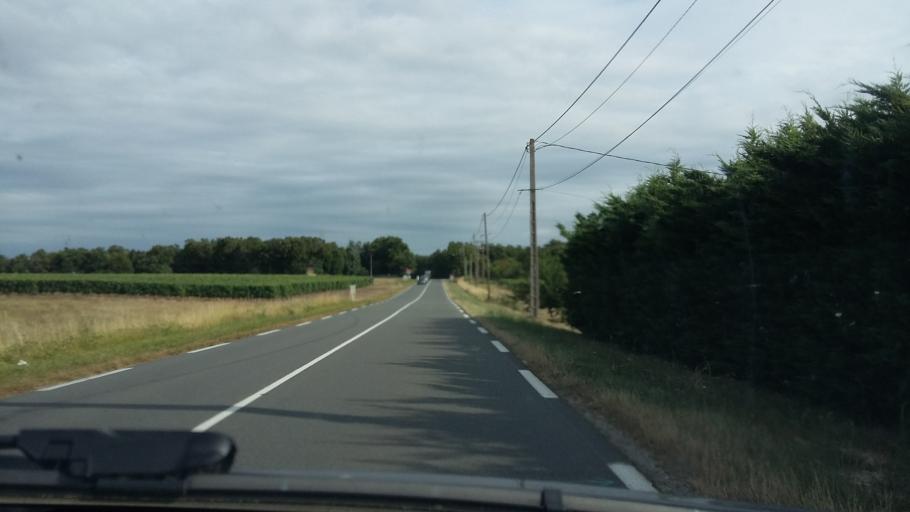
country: FR
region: Poitou-Charentes
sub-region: Departement de la Charente
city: Balzac
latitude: 45.6972
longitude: 0.0975
